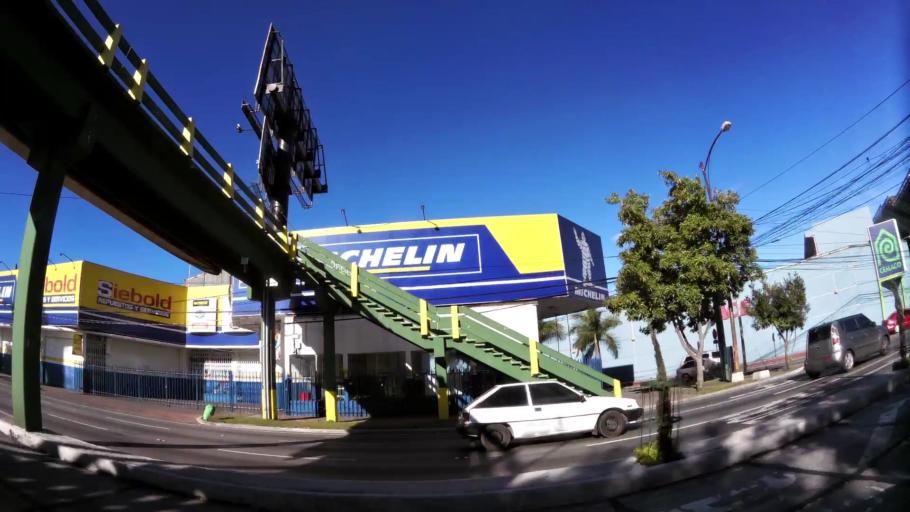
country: GT
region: Guatemala
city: Guatemala City
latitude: 14.6222
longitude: -90.5151
